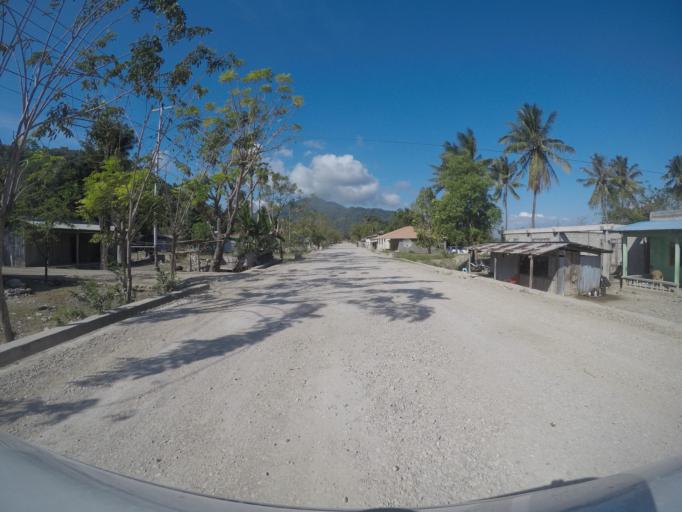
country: TL
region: Viqueque
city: Viqueque
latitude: -8.8039
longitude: 126.5476
